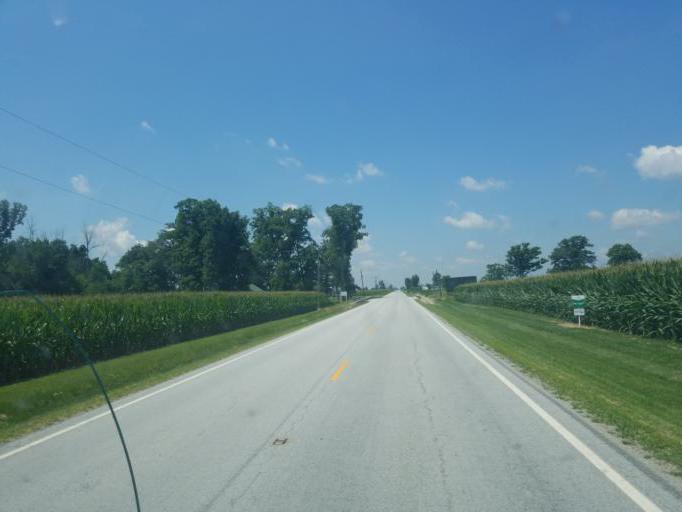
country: US
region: Ohio
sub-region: Allen County
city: Spencerville
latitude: 40.7142
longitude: -84.3702
